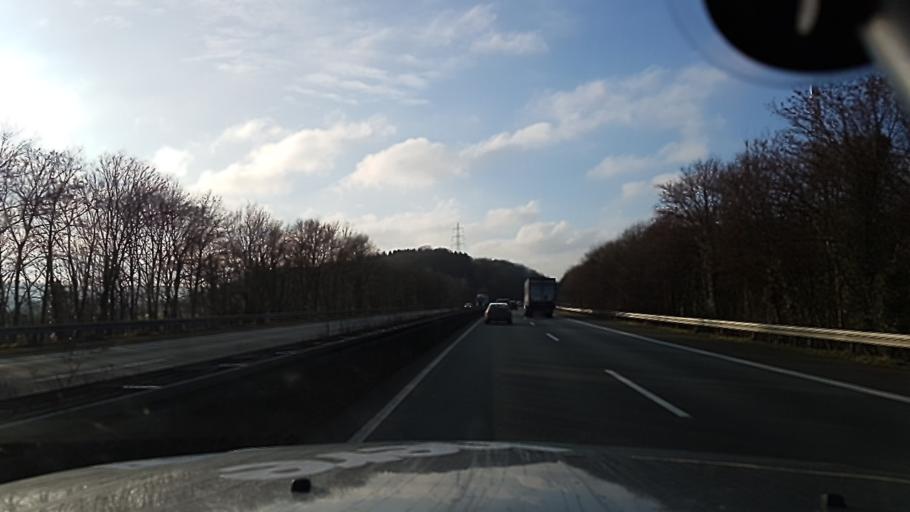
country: DE
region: North Rhine-Westphalia
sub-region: Regierungsbezirk Munster
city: Tecklenburg
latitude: 52.2539
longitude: 7.8137
